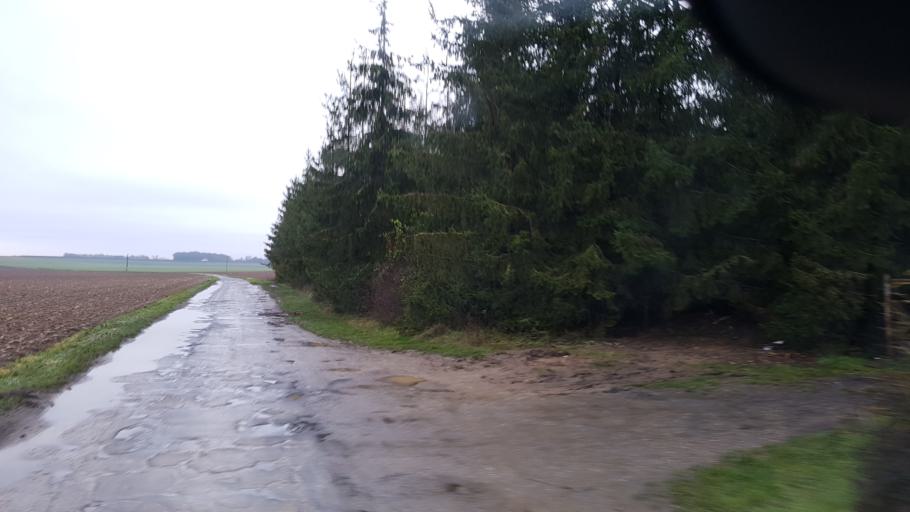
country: FR
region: Ile-de-France
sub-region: Departement de l'Essonne
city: Etampes
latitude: 48.4140
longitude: 2.1370
